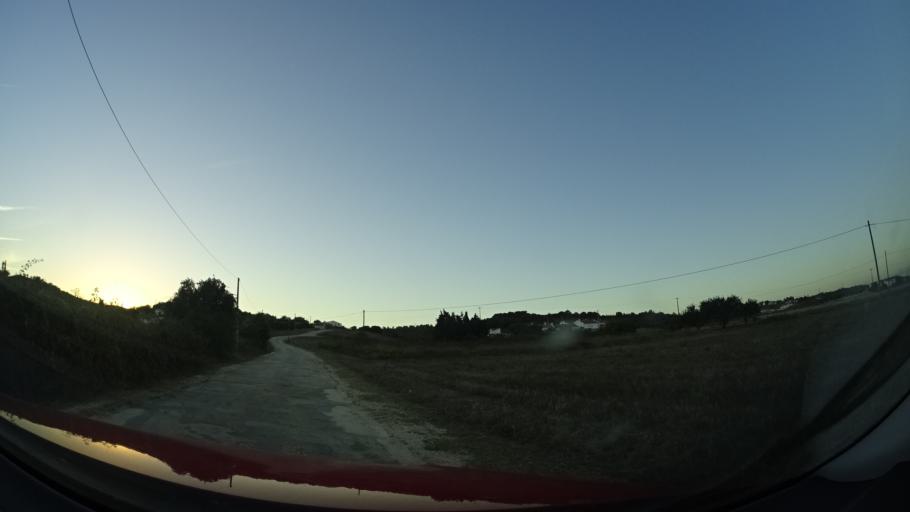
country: PT
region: Faro
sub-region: Aljezur
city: Aljezur
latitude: 37.2379
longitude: -8.8296
